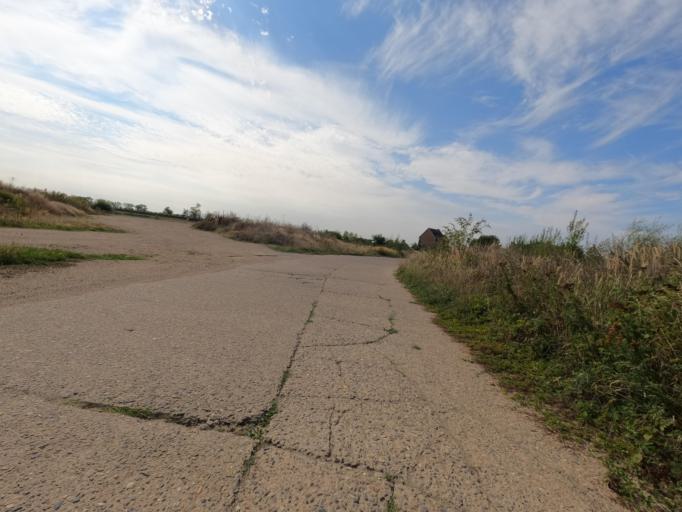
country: BE
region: Flanders
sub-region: Provincie Limburg
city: Maaseik
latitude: 51.0959
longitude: 5.8008
